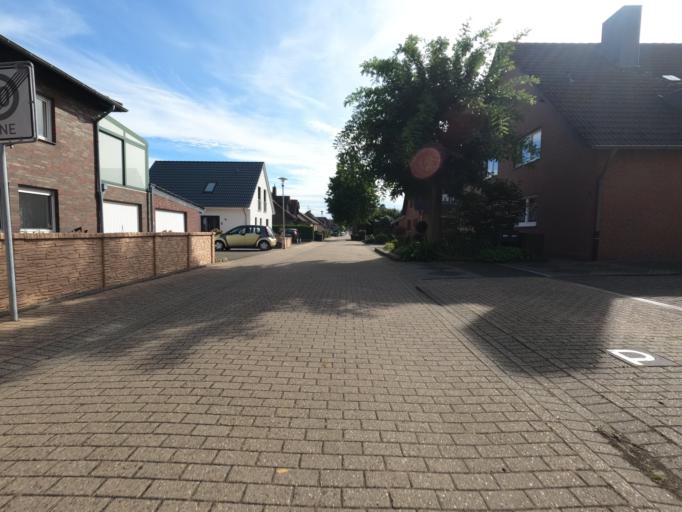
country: DE
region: North Rhine-Westphalia
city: Baesweiler
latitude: 50.9319
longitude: 6.1919
